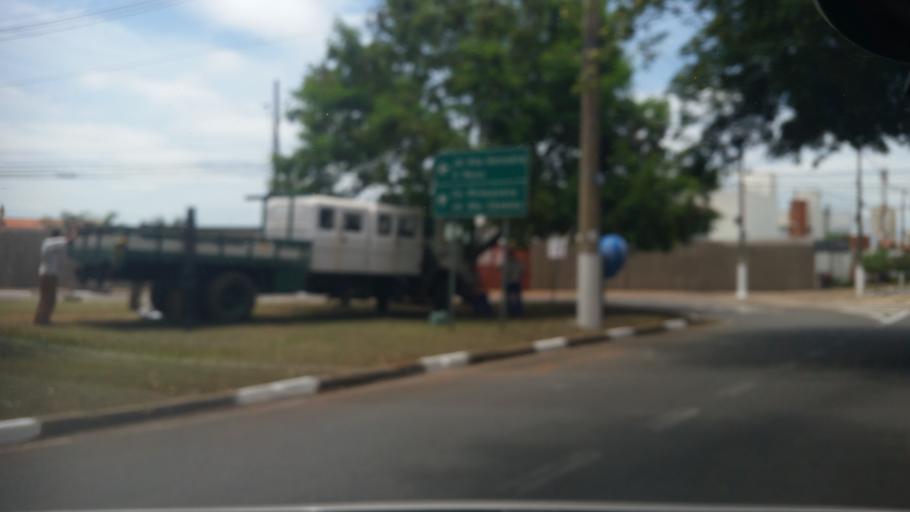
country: BR
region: Sao Paulo
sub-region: Campinas
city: Campinas
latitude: -22.8641
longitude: -47.0526
